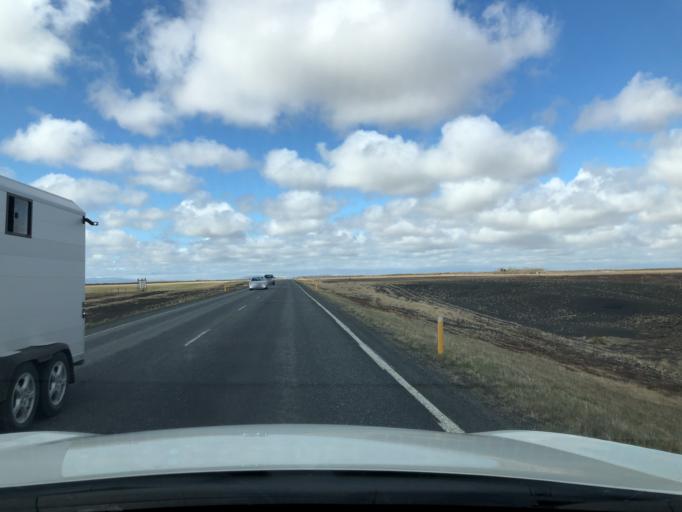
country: IS
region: South
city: Vestmannaeyjar
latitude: 63.7992
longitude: -20.3190
